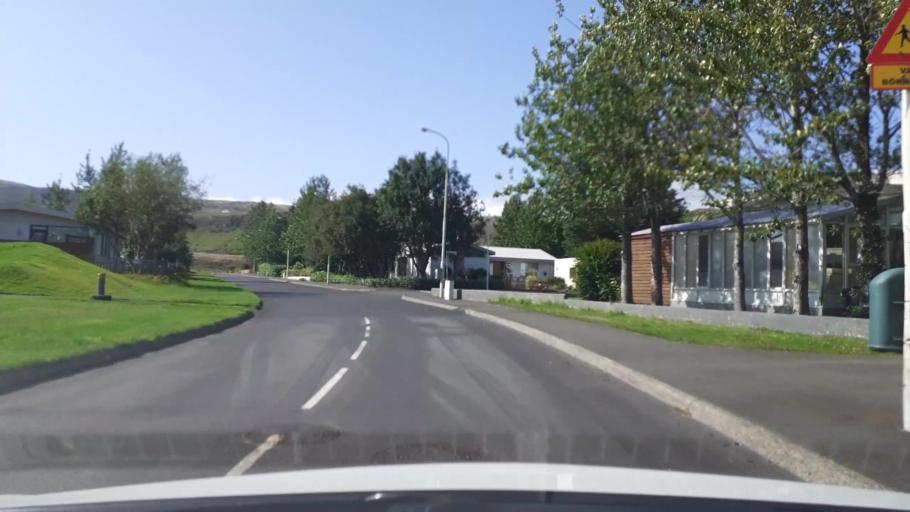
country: IS
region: South
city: Hveragerdi
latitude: 64.0035
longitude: -21.2006
